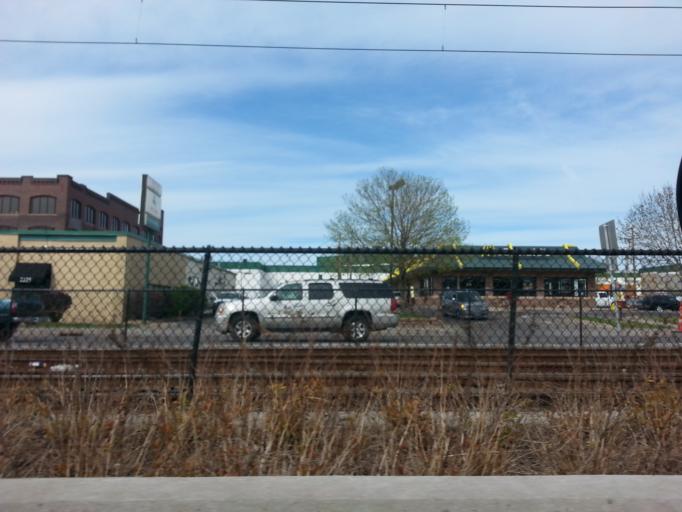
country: US
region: Minnesota
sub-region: Ramsey County
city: Lauderdale
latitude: 44.9616
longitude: -93.1920
